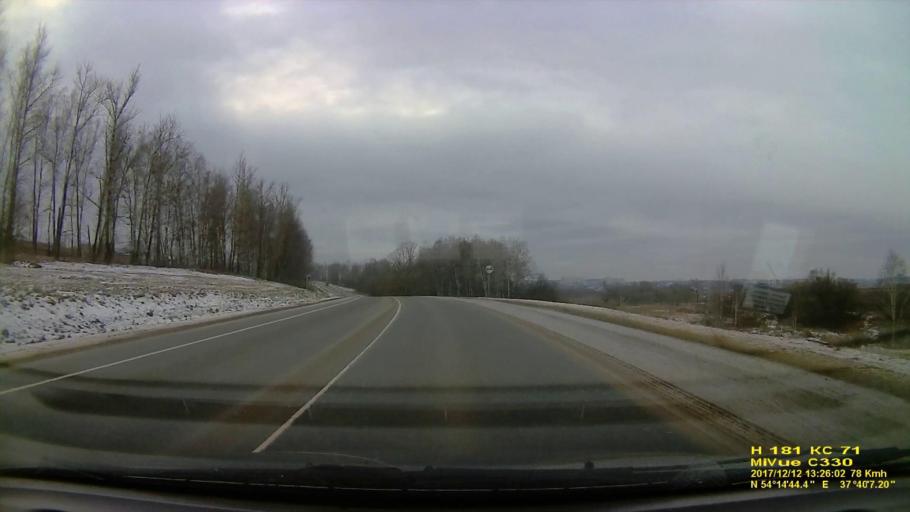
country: RU
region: Tula
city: Gorelki
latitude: 54.2457
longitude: 37.6687
